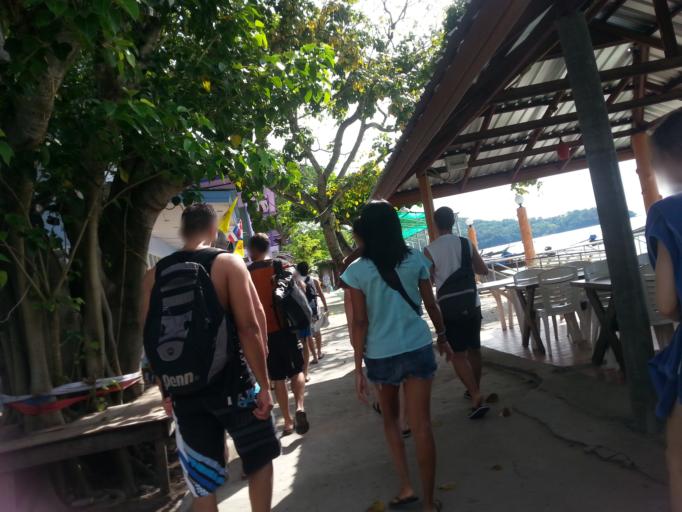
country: TH
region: Phangnga
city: Ban Phru Nai
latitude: 7.7364
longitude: 98.7748
